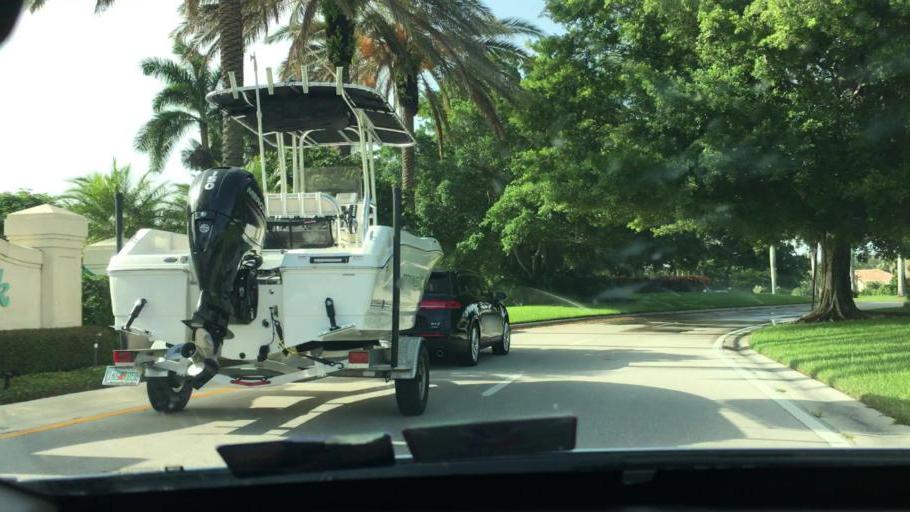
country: US
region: Florida
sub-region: Palm Beach County
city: Plantation Mobile Home Park
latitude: 26.7085
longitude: -80.1571
